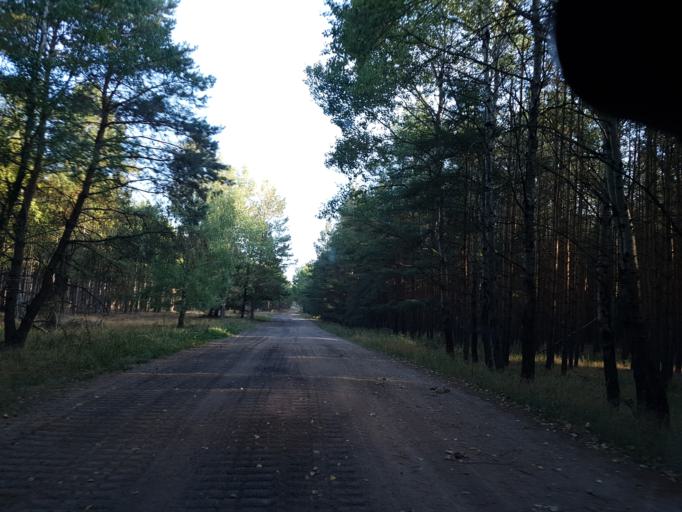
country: DE
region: Brandenburg
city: Niedergorsdorf
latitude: 52.0198
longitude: 12.9253
